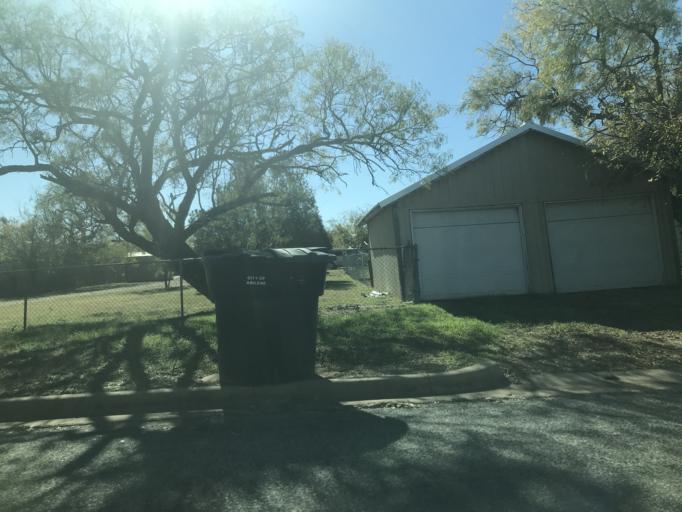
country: US
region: Texas
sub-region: Taylor County
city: Abilene
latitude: 32.4706
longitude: -99.7460
